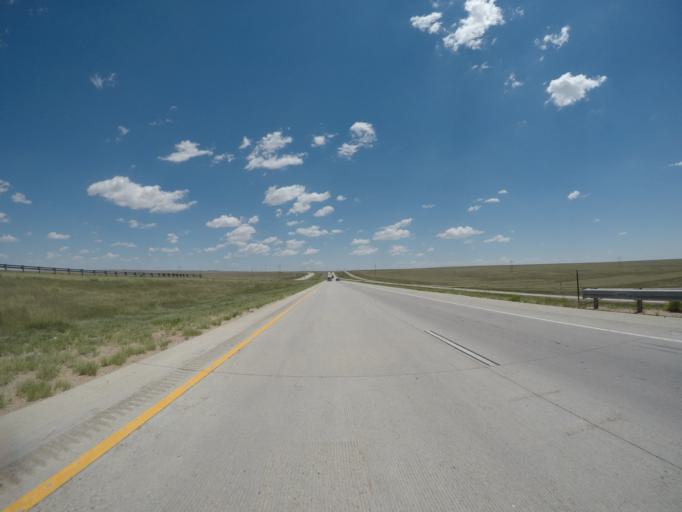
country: US
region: Colorado
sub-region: Lincoln County
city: Limon
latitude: 39.2629
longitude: -103.6461
